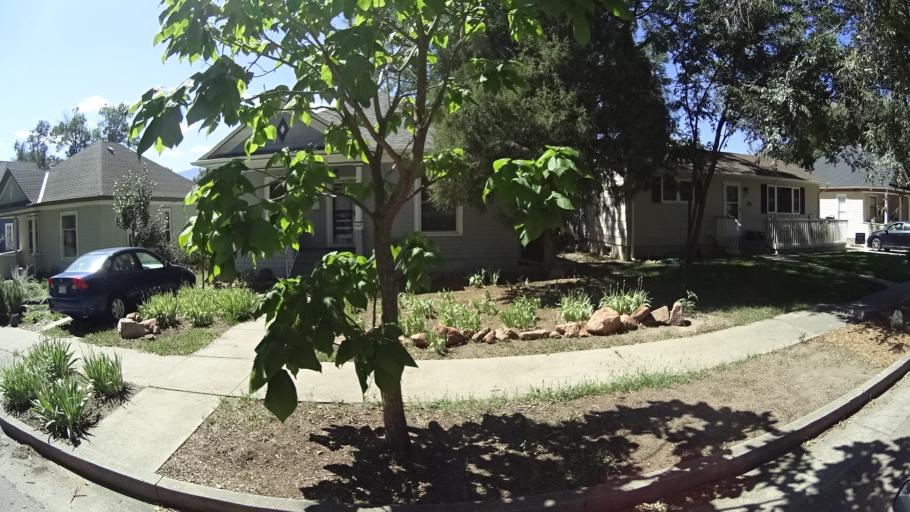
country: US
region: Colorado
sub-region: El Paso County
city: Colorado Springs
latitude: 38.8402
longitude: -104.8116
